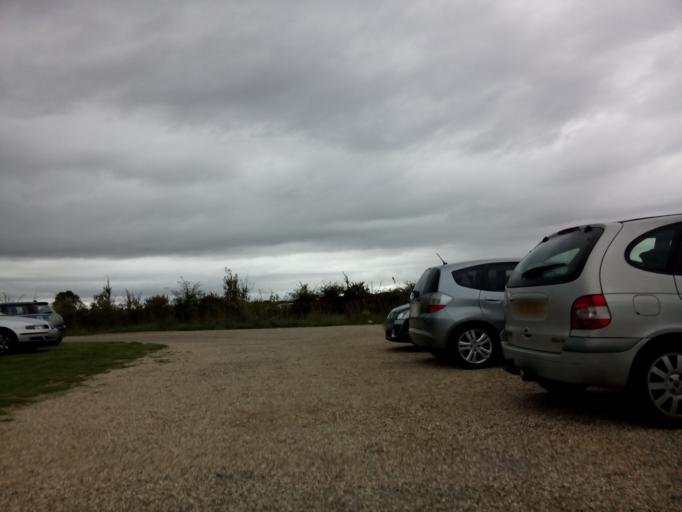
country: GB
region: England
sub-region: Suffolk
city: Ipswich
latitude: 52.0189
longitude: 1.1235
